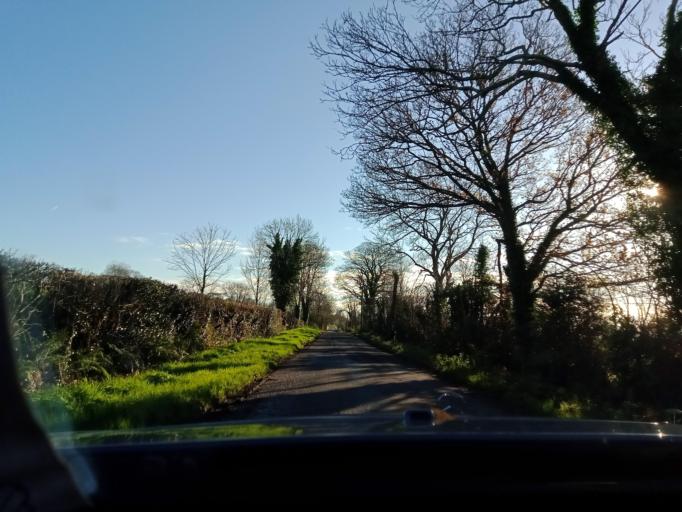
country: IE
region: Leinster
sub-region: Kilkenny
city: Mooncoin
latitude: 52.3410
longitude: -7.2701
